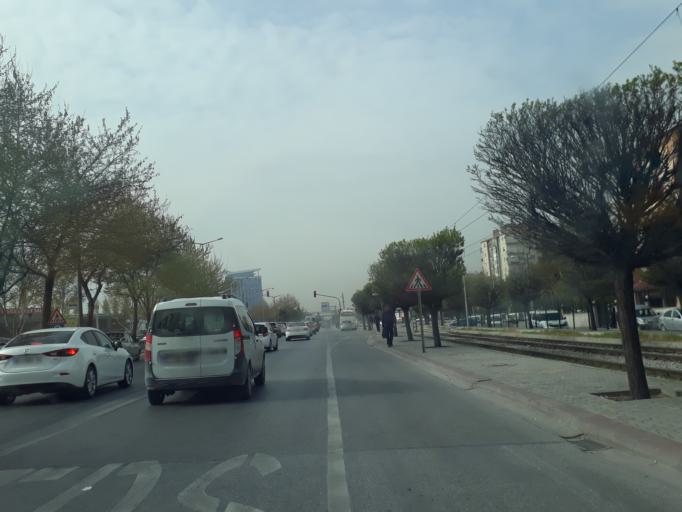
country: TR
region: Konya
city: Selcuklu
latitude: 37.9430
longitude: 32.5119
